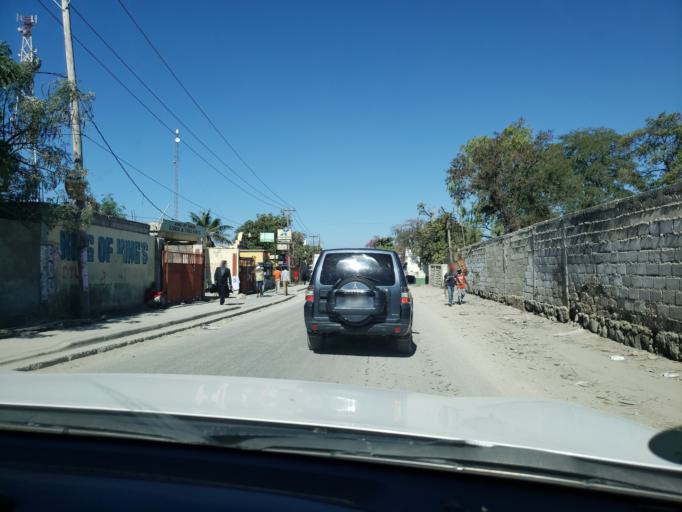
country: HT
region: Ouest
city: Croix des Bouquets
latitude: 18.5752
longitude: -72.2288
